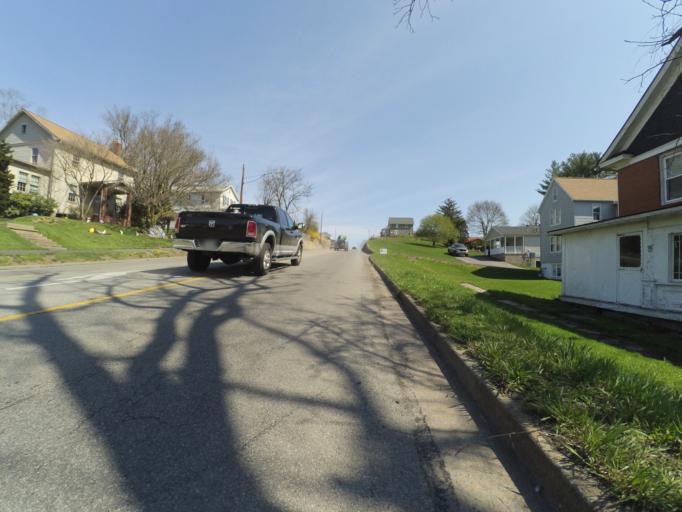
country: US
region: Pennsylvania
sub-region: Clinton County
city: Flemington
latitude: 41.1262
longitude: -77.4695
